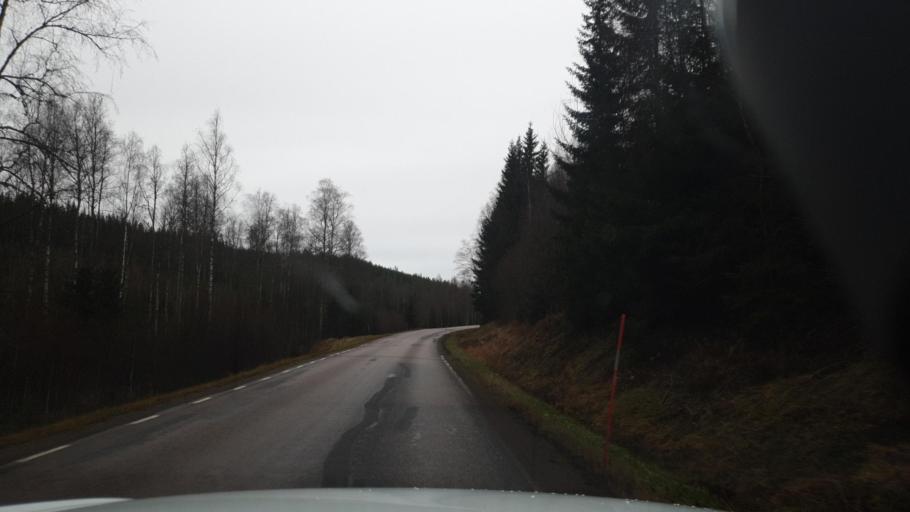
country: SE
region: Vaermland
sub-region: Arvika Kommun
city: Arvika
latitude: 59.7151
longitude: 12.7961
